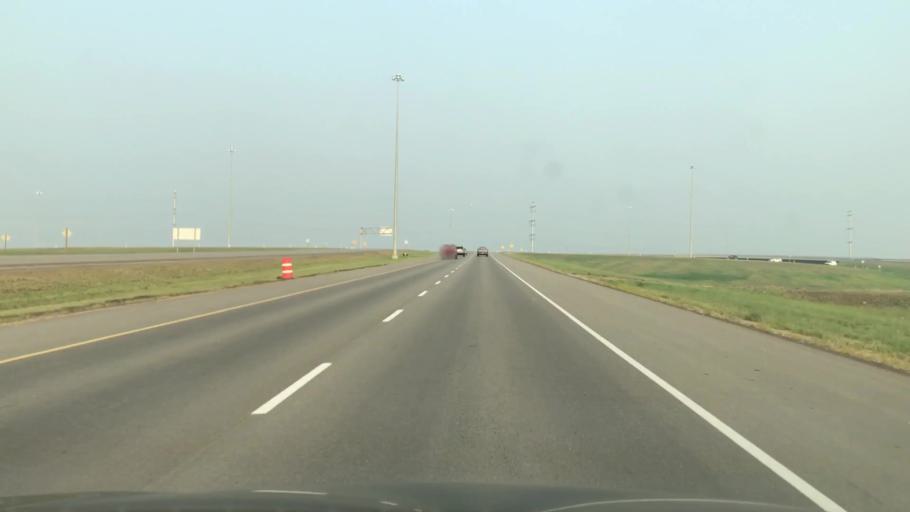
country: CA
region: Alberta
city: Sherwood Park
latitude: 53.5139
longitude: -113.3512
